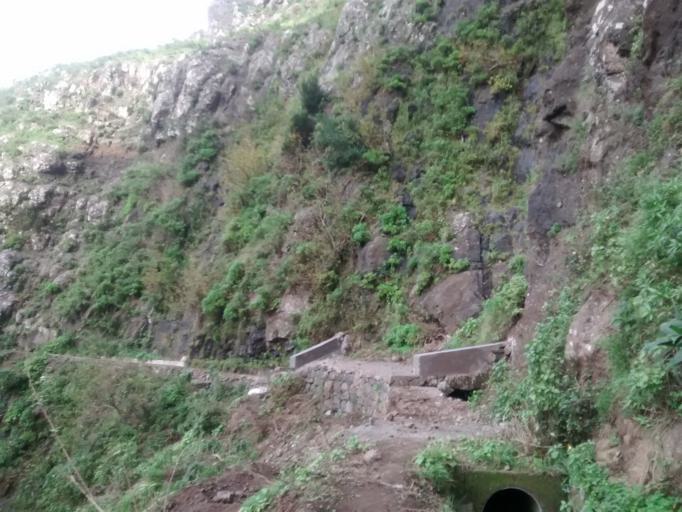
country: PT
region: Madeira
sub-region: Camara de Lobos
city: Curral das Freiras
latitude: 32.7197
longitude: -17.0243
